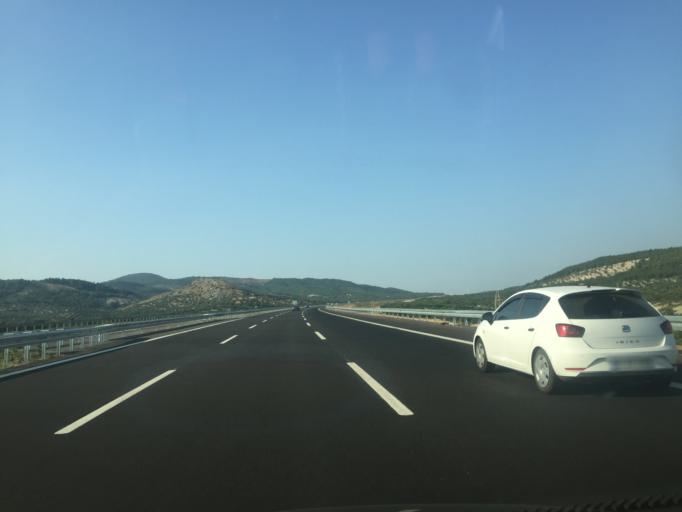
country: TR
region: Manisa
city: Zeytinliova
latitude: 38.9823
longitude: 27.7314
